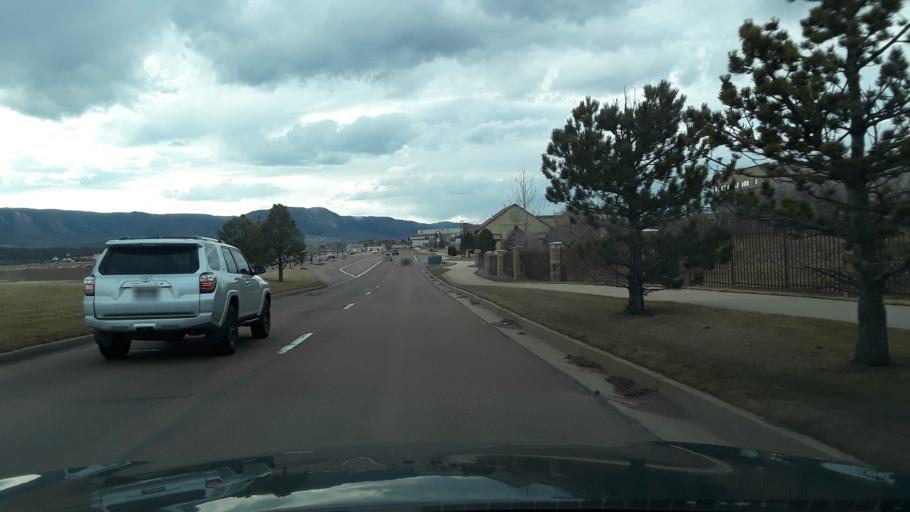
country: US
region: Colorado
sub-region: El Paso County
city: Gleneagle
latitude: 39.0192
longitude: -104.8115
